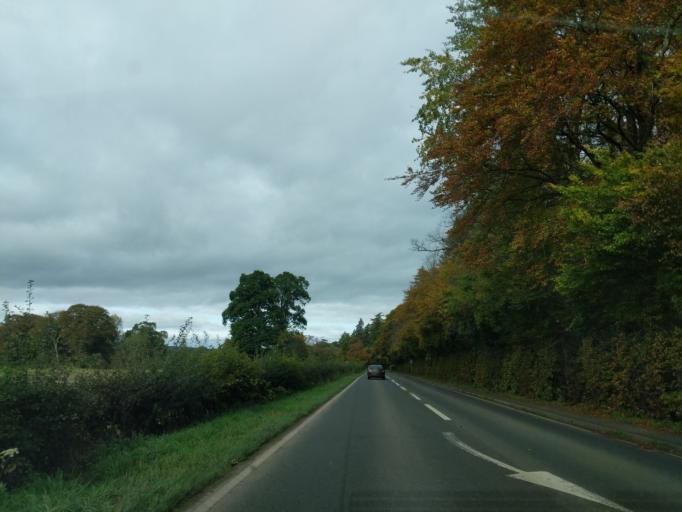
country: GB
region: Scotland
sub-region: Dumfries and Galloway
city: Thornhill
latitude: 55.2549
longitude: -3.7746
